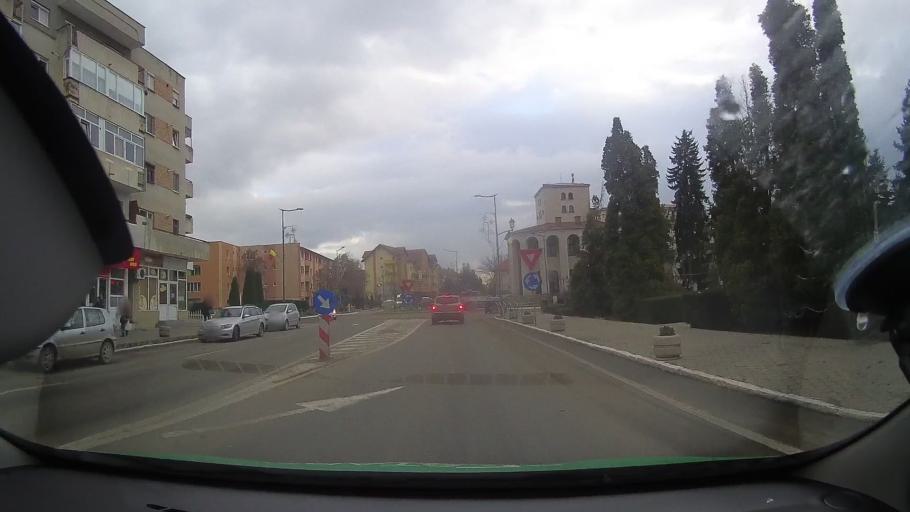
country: RO
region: Cluj
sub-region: Municipiul Campia Turzii
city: Campia Turzii
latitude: 46.5431
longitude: 23.8881
